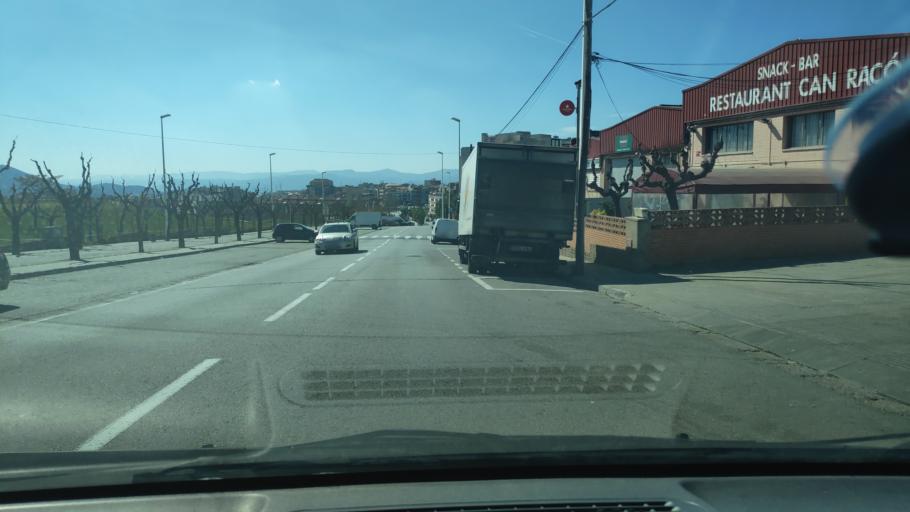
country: ES
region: Catalonia
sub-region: Provincia de Barcelona
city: Rubi
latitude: 41.5022
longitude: 2.0423
